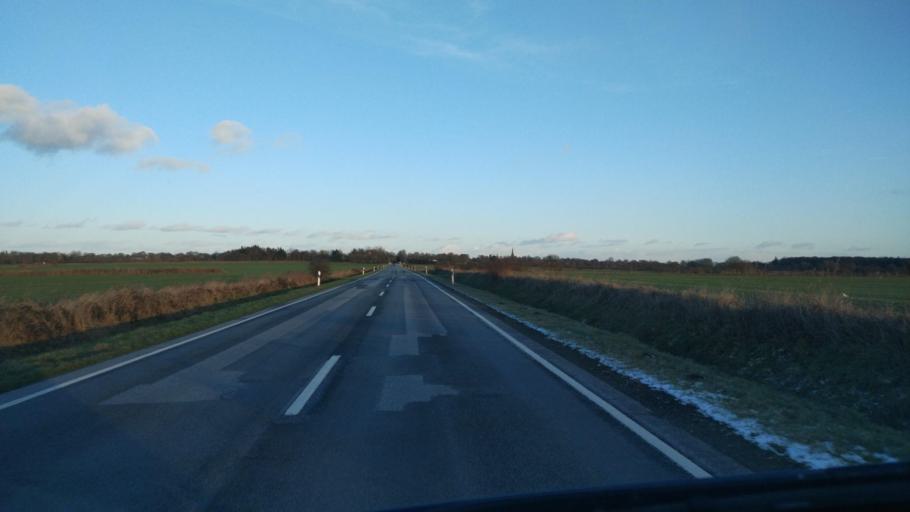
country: DE
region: Schleswig-Holstein
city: Wittbek
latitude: 54.4623
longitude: 9.2077
